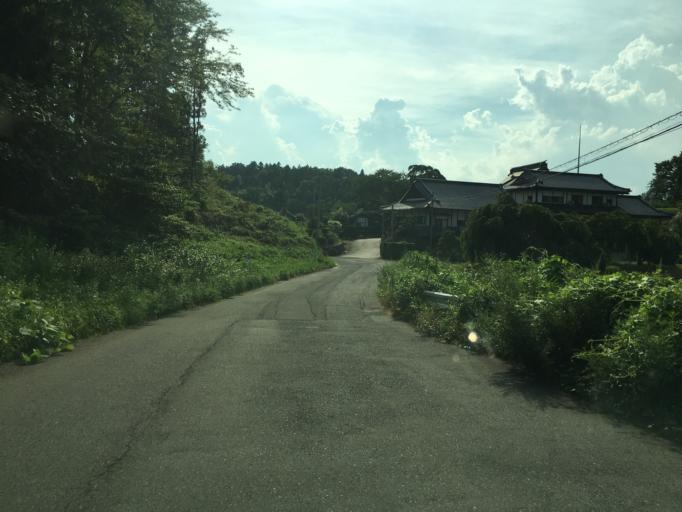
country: JP
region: Fukushima
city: Miharu
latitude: 37.4186
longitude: 140.4455
